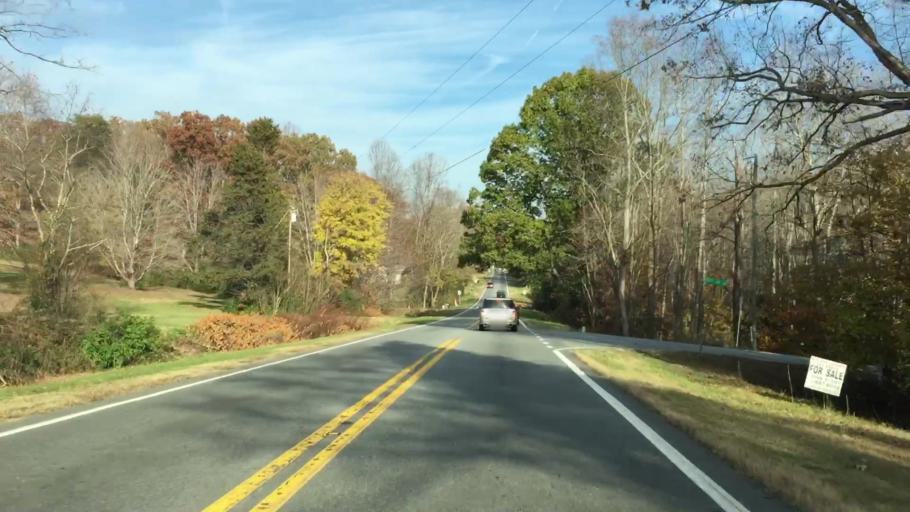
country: US
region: North Carolina
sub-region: Guilford County
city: Stokesdale
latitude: 36.2412
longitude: -79.9976
